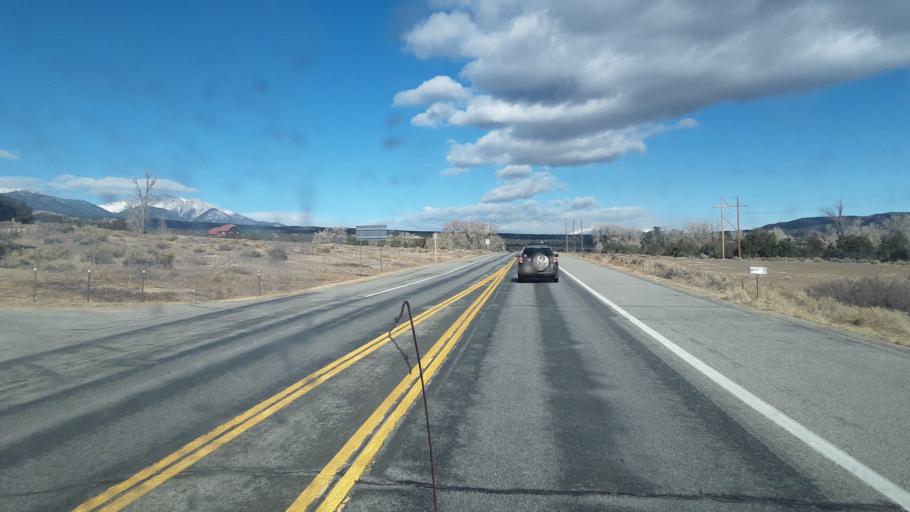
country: US
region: Colorado
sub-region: Chaffee County
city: Salida
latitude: 38.5787
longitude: -106.0819
